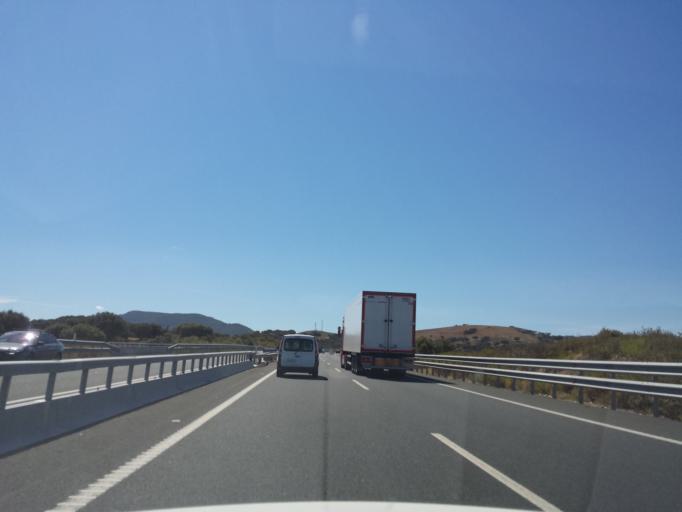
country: ES
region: Extremadura
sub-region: Provincia de Caceres
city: Casas de Miravete
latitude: 39.7681
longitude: -5.7360
